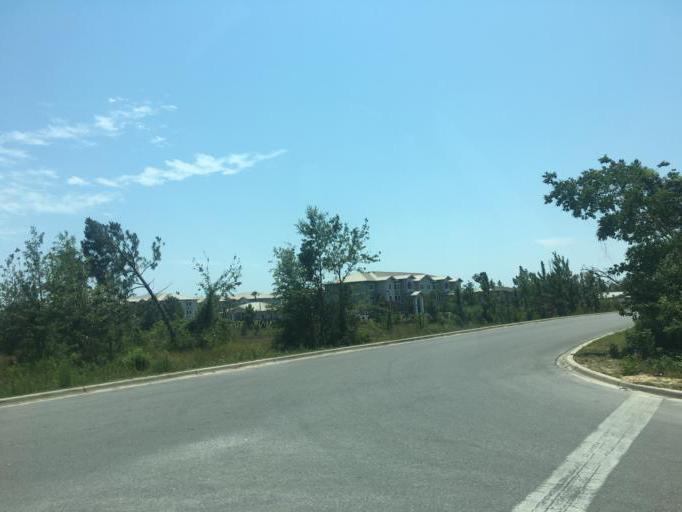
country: US
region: Florida
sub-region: Bay County
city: Lynn Haven
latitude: 30.2256
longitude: -85.6512
